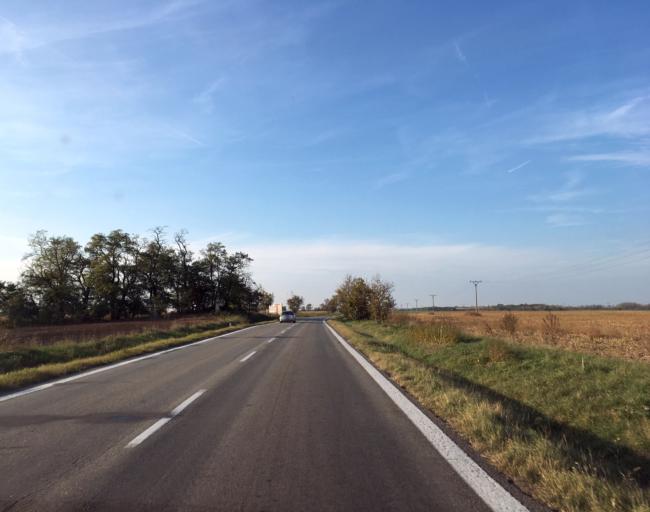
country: SK
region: Nitriansky
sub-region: Okres Nove Zamky
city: Nove Zamky
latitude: 48.0342
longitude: 18.1284
